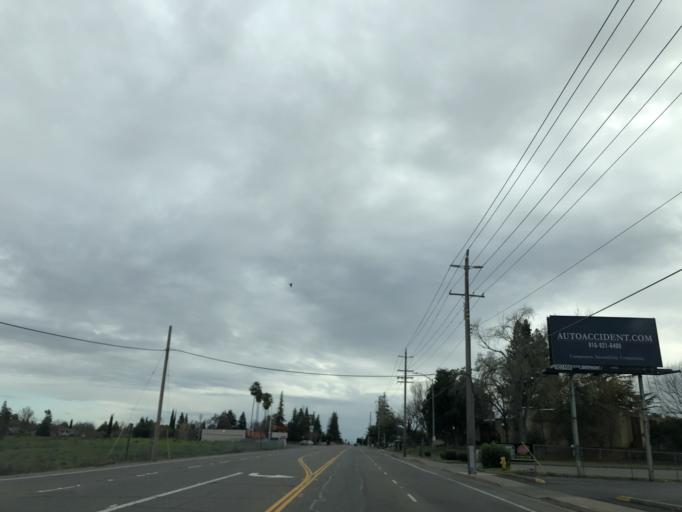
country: US
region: California
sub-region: Sacramento County
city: Carmichael
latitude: 38.6479
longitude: -121.3279
